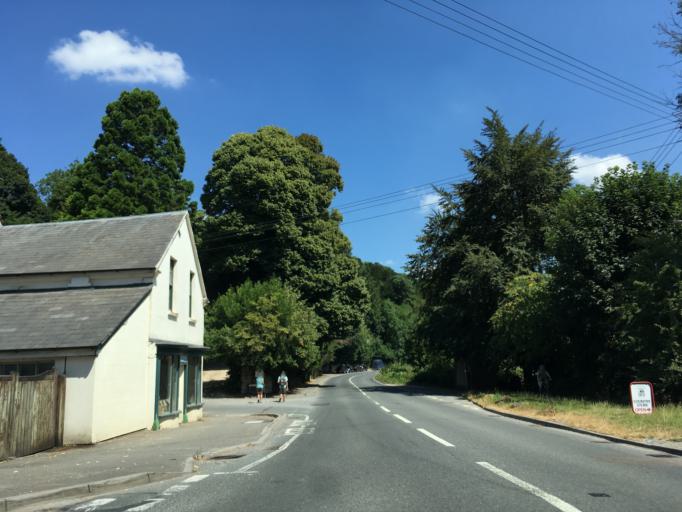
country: GB
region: England
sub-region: Gloucestershire
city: Chalford
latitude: 51.7215
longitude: -2.1575
